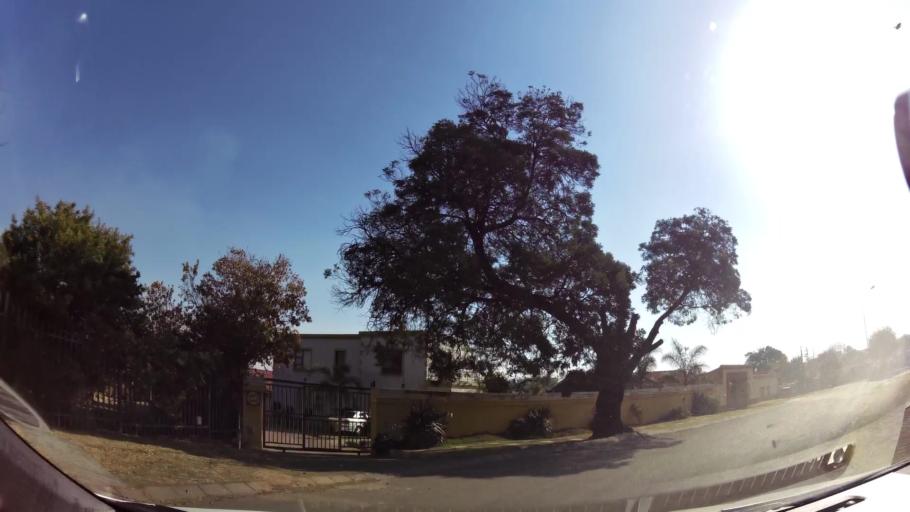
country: ZA
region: Gauteng
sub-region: City of Johannesburg Metropolitan Municipality
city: Johannesburg
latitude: -26.2596
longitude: 27.9905
